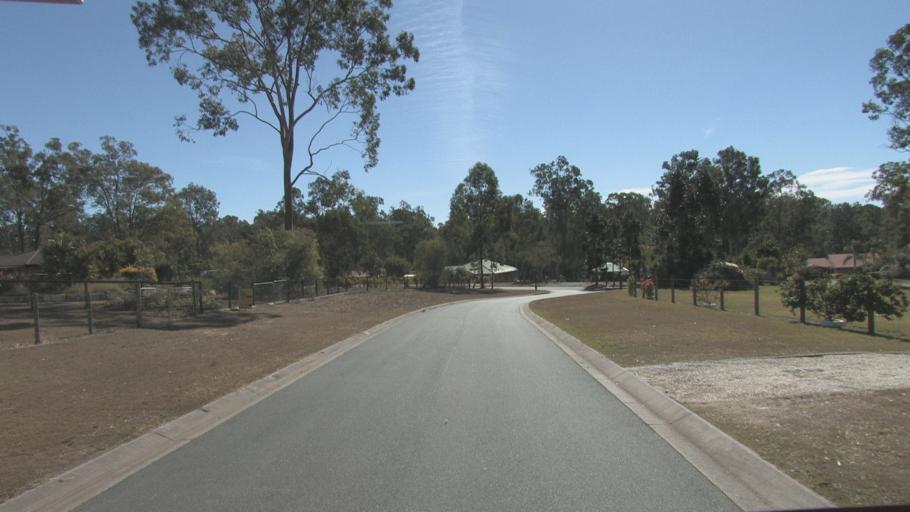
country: AU
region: Queensland
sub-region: Logan
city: North Maclean
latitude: -27.8177
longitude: 152.9592
